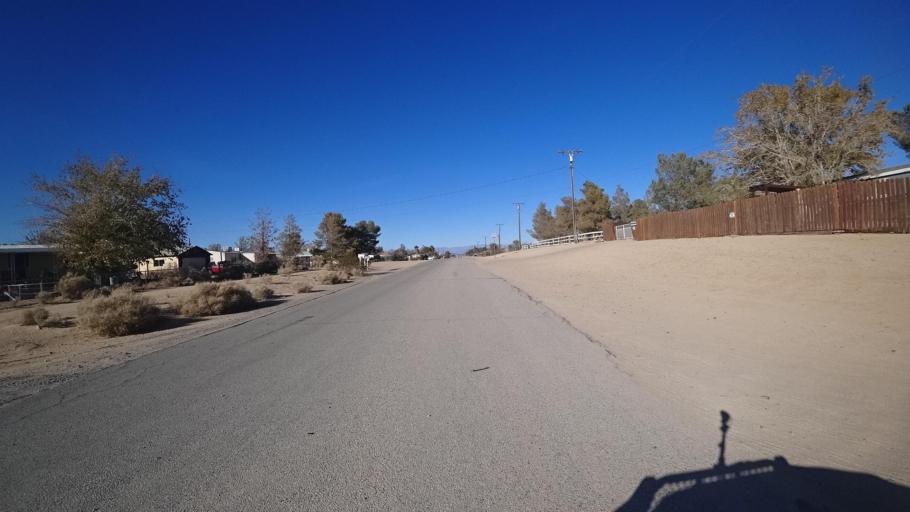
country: US
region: California
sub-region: Kern County
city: China Lake Acres
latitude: 35.6391
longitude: -117.7586
